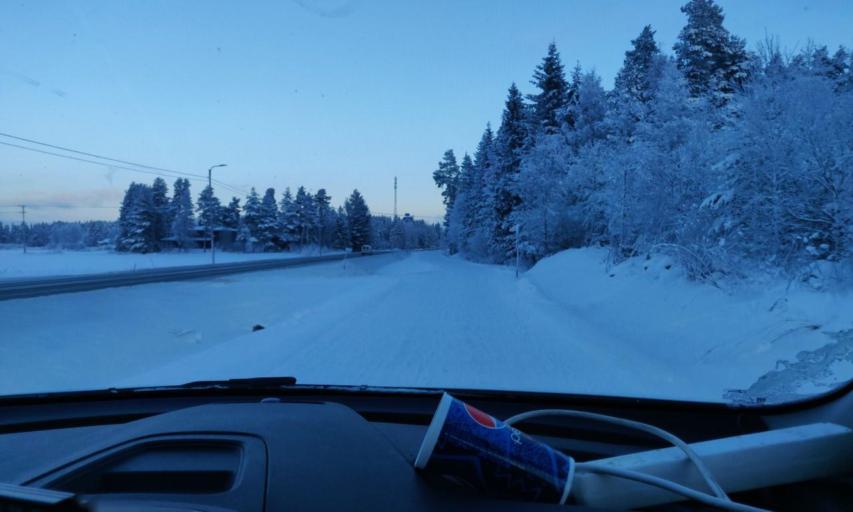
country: FI
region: Northern Ostrobothnia
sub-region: Ylivieska
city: Ylivieska
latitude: 64.0651
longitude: 24.4965
